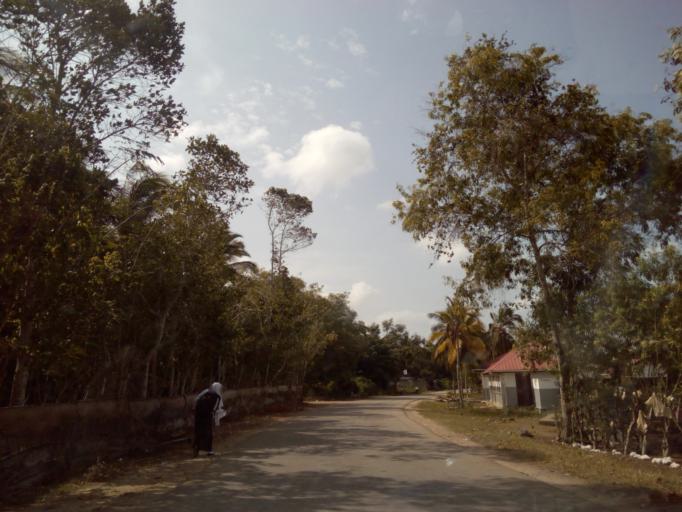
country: TZ
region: Zanzibar Central/South
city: Koani
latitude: -6.2885
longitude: 39.3708
